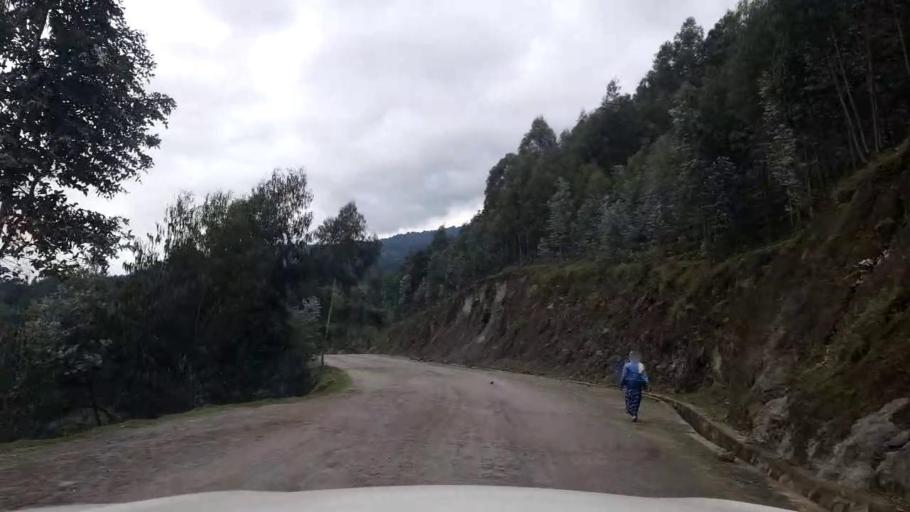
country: RW
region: Northern Province
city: Musanze
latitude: -1.5238
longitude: 29.5325
